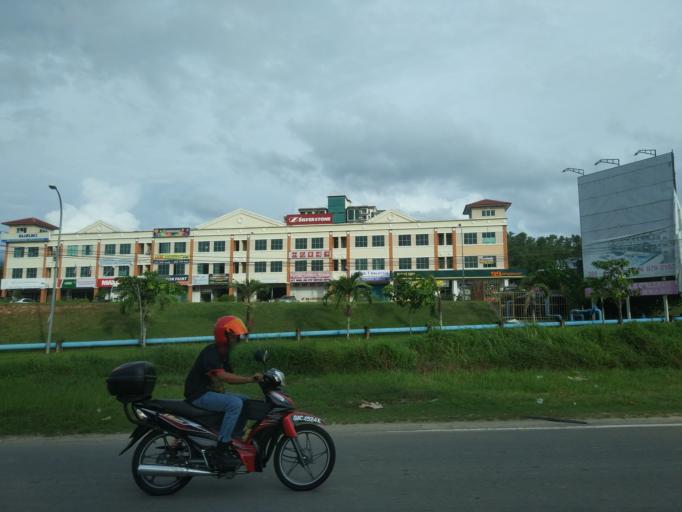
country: MY
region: Sabah
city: Kota Kinabalu
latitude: 6.0176
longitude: 116.1385
